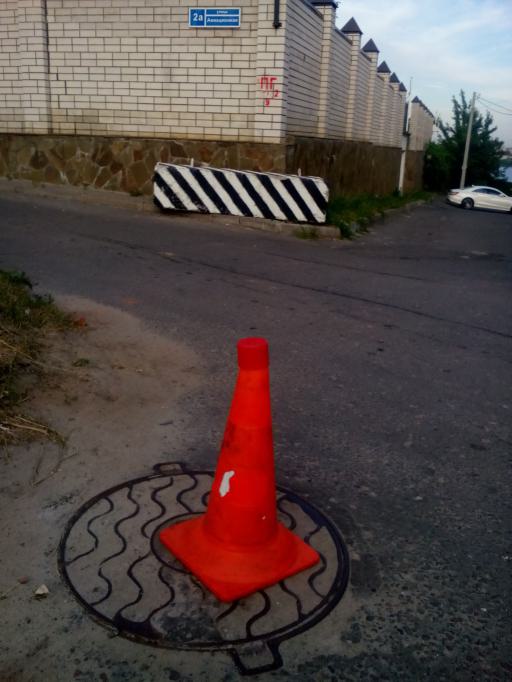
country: RU
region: Voronezj
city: Voronezh
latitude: 51.6630
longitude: 39.2170
